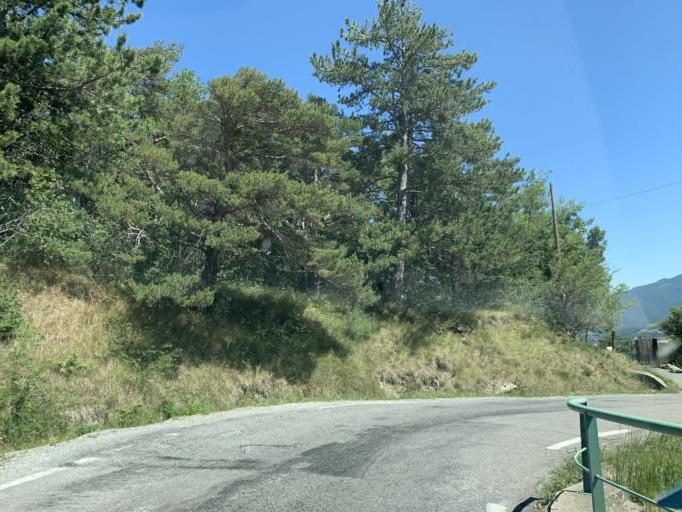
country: FR
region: Provence-Alpes-Cote d'Azur
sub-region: Departement des Hautes-Alpes
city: La Batie-Neuve
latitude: 44.5899
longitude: 6.1557
